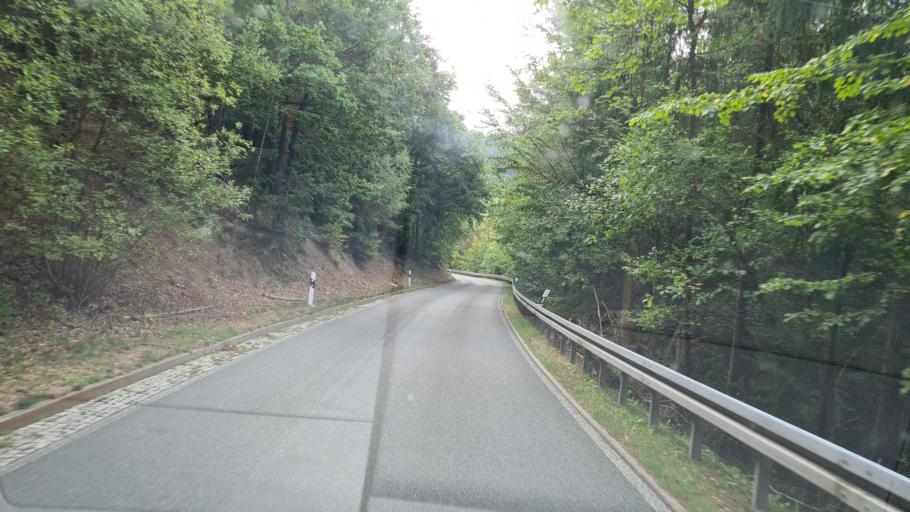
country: DE
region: Thuringia
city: Leutenberg
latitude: 50.5607
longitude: 11.4290
